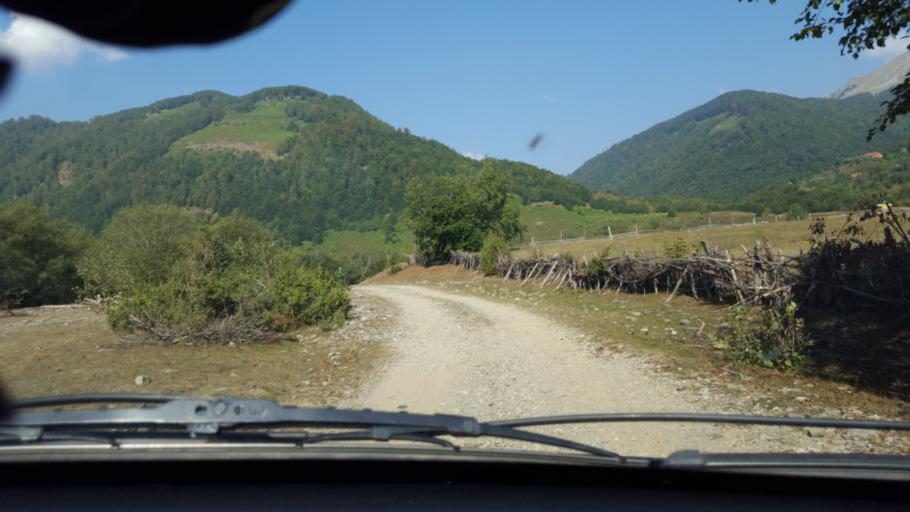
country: ME
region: Andrijevica
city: Andrijevica
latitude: 42.5967
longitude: 19.6606
